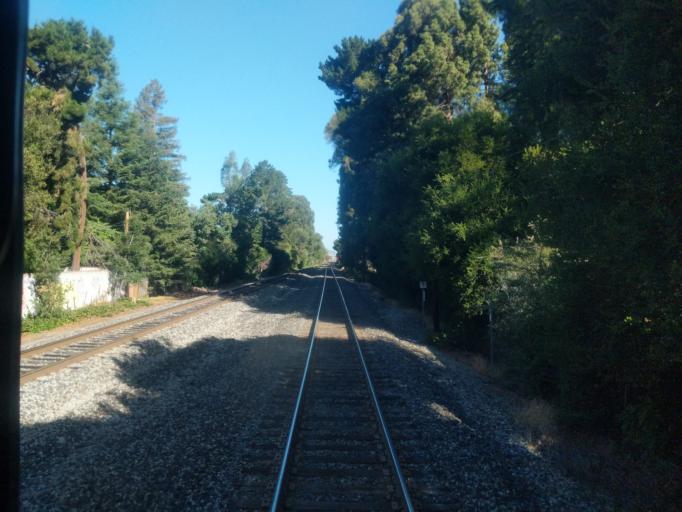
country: US
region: California
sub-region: San Mateo County
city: Atherton
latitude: 37.4660
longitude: -122.1998
